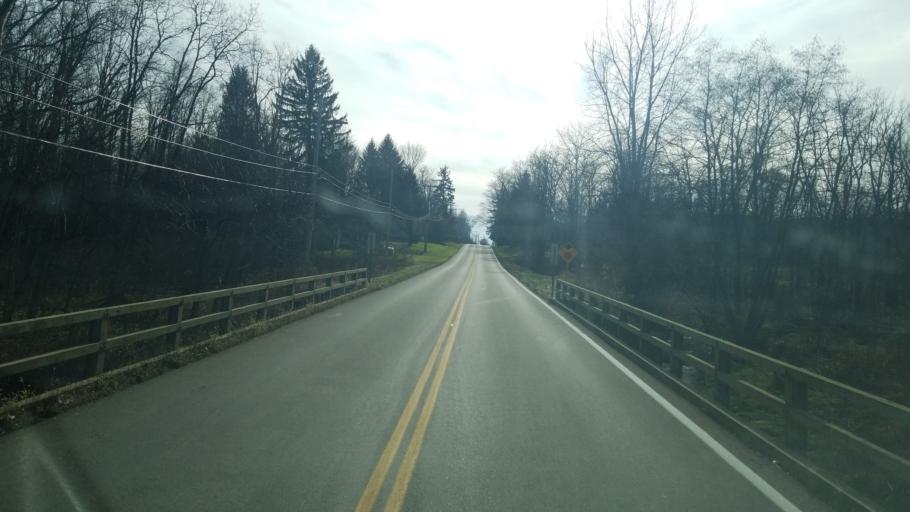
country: US
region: Ohio
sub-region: Ashtabula County
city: Roaming Shores
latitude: 41.6642
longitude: -80.9145
